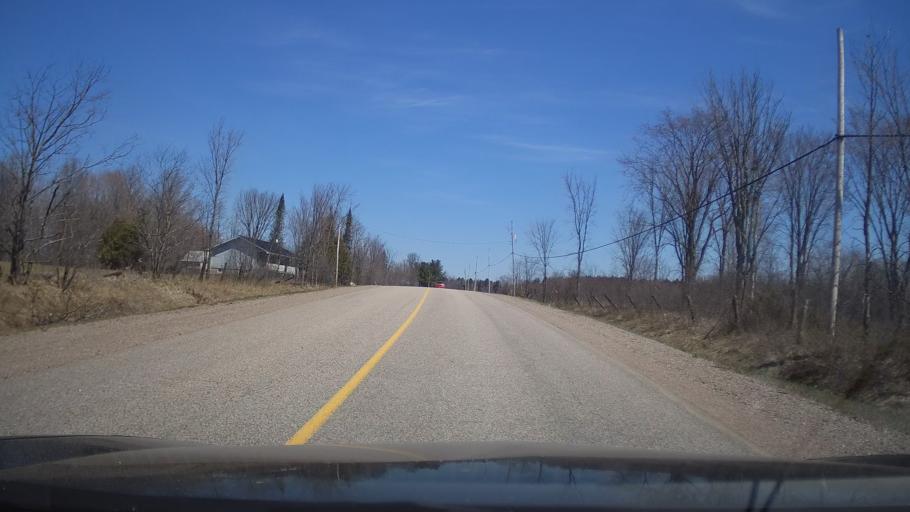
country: CA
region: Ontario
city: Arnprior
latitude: 45.5355
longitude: -76.3696
